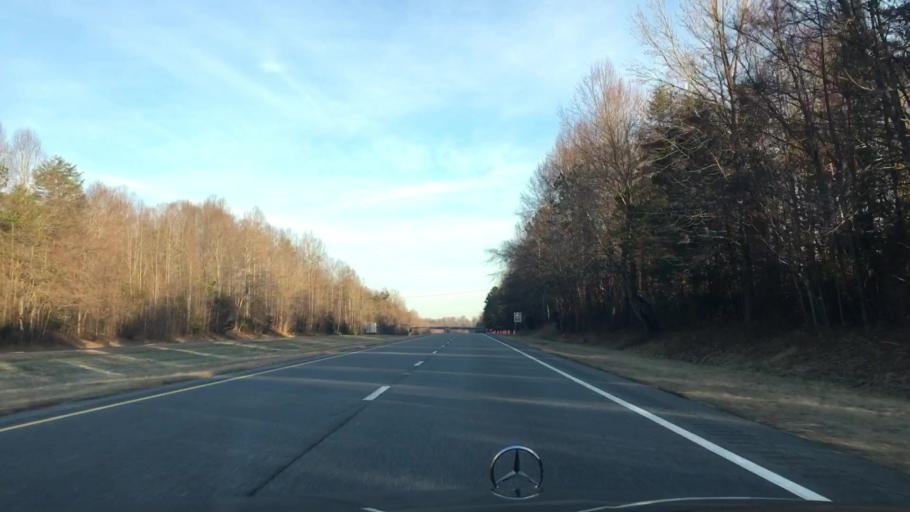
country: US
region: North Carolina
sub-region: Guilford County
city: Pleasant Garden
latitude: 36.0080
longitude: -79.7583
